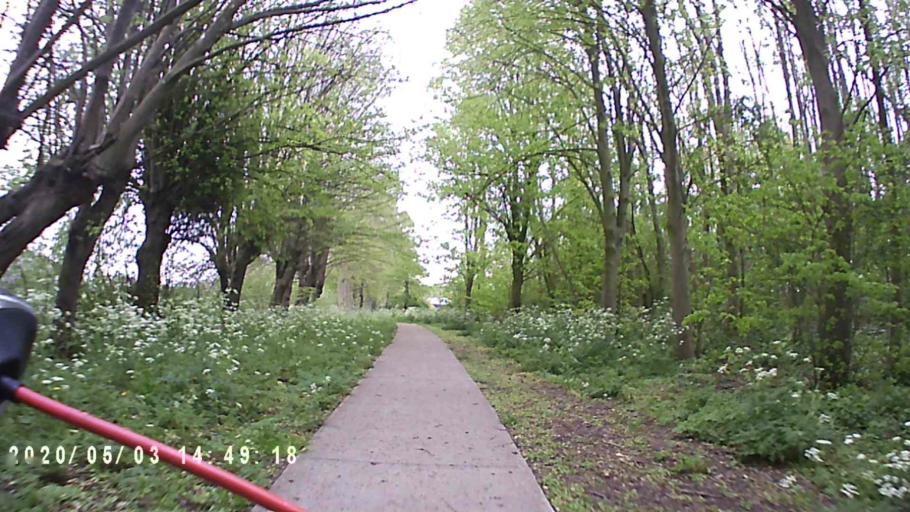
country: NL
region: Groningen
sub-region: Gemeente Zuidhorn
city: Oldehove
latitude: 53.3630
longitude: 6.4124
